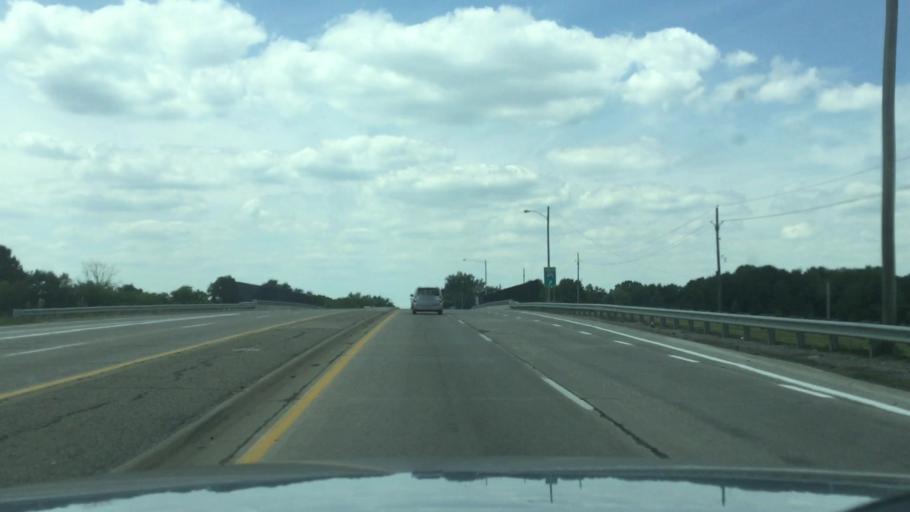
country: US
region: Michigan
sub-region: Genesee County
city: Grand Blanc
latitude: 42.9441
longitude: -83.6800
